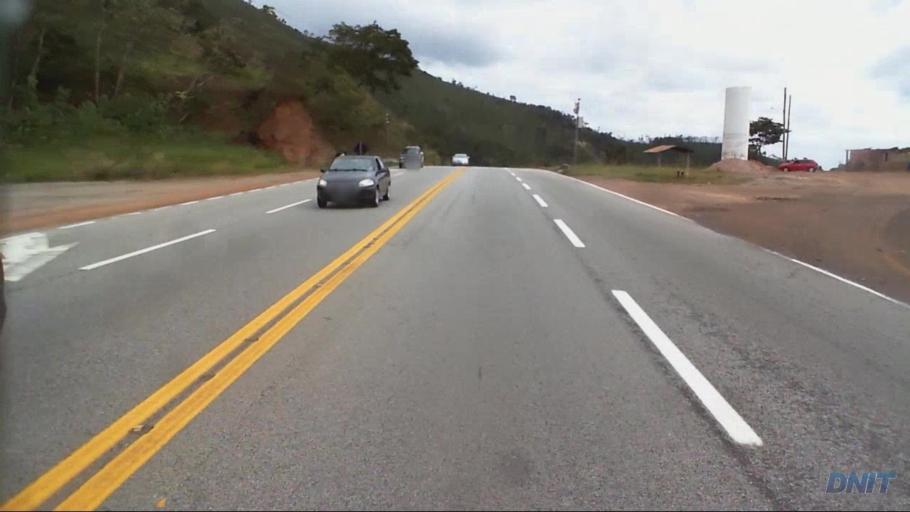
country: BR
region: Minas Gerais
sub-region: Caete
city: Caete
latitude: -19.7877
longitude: -43.6934
